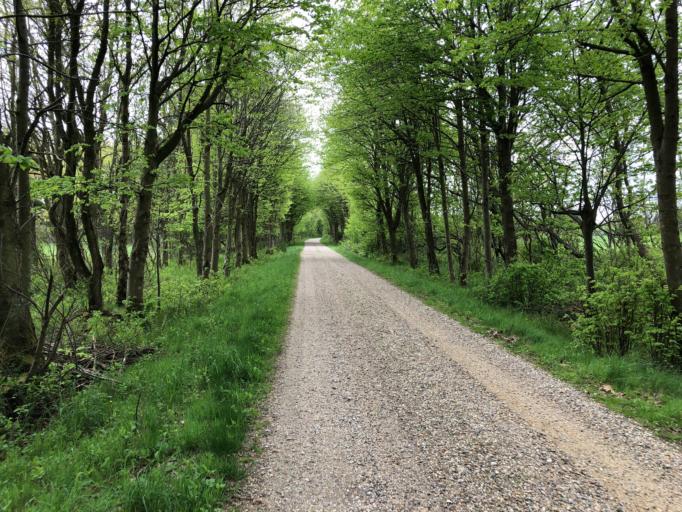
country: DK
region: Central Jutland
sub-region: Holstebro Kommune
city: Ulfborg
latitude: 56.2721
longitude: 8.4304
